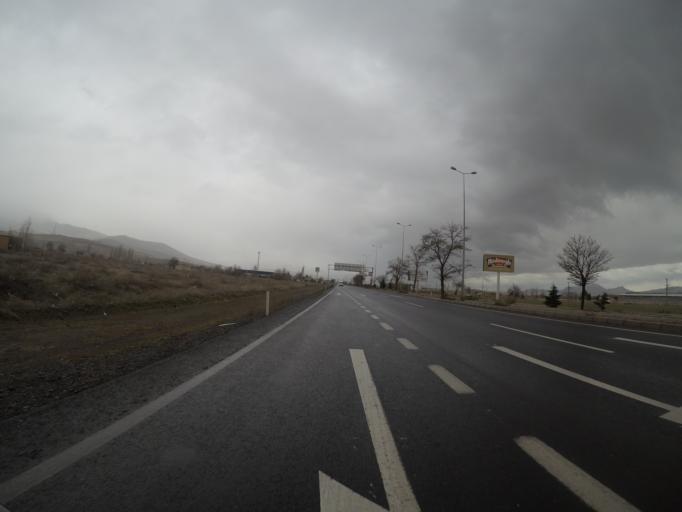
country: TR
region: Kayseri
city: Incesu
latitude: 38.6825
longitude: 35.2358
